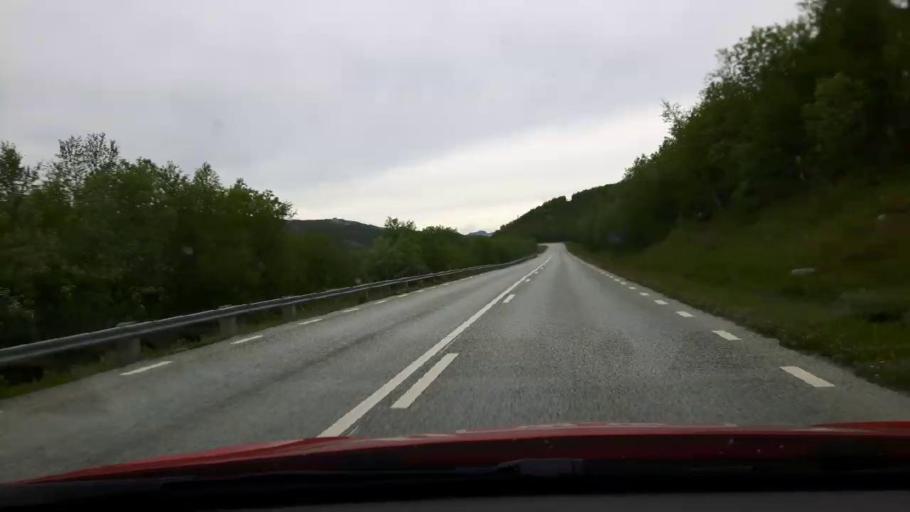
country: NO
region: Sor-Trondelag
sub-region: Tydal
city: Aas
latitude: 62.5571
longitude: 12.2721
